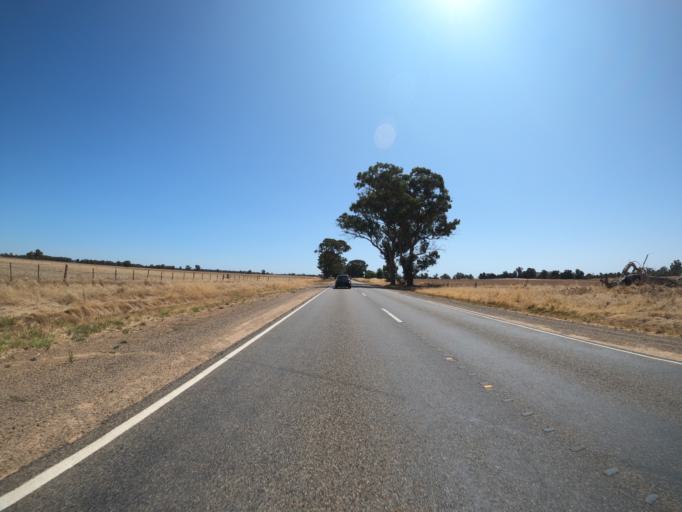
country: AU
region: Victoria
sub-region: Moira
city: Yarrawonga
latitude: -36.0237
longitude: 146.1155
